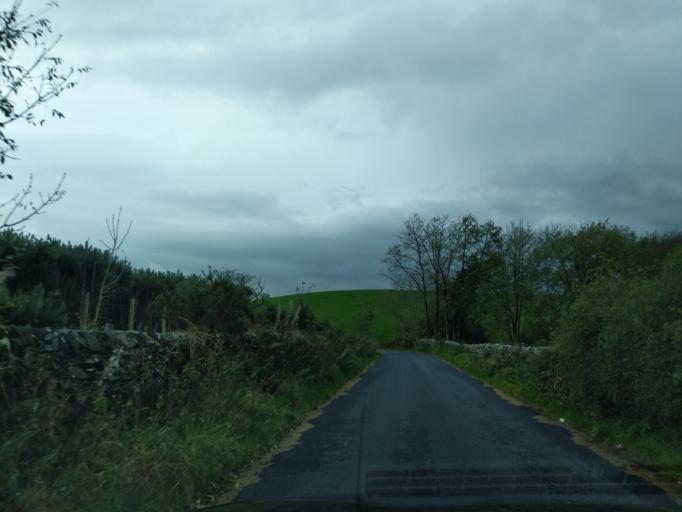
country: GB
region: Scotland
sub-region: Dumfries and Galloway
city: Castle Douglas
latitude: 54.9236
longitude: -3.9549
